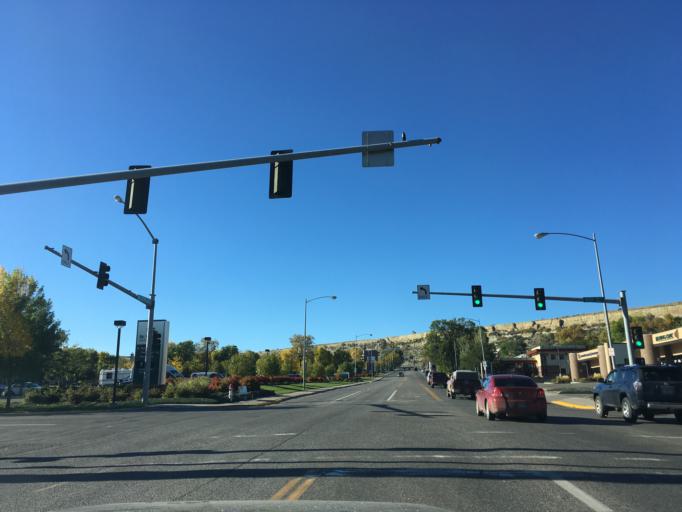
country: US
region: Montana
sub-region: Yellowstone County
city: Billings
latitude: 45.7924
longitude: -108.5141
